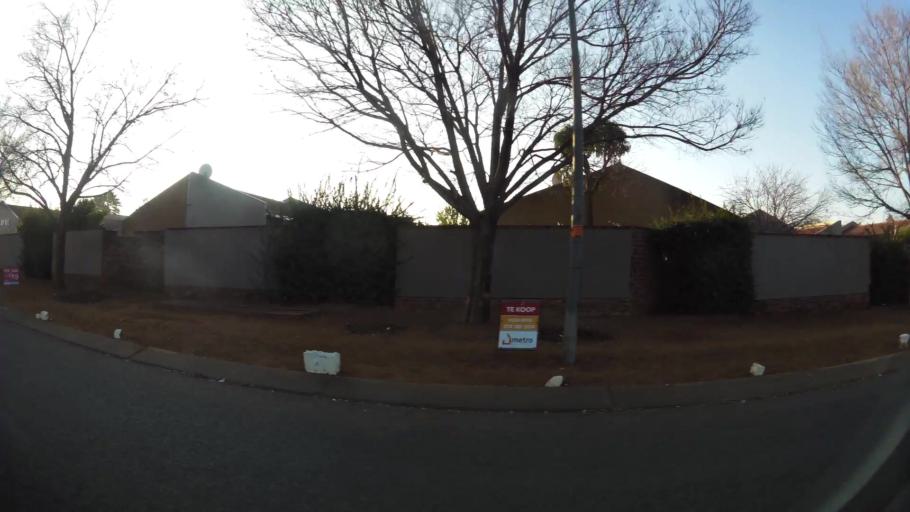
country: ZA
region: Orange Free State
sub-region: Mangaung Metropolitan Municipality
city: Bloemfontein
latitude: -29.1012
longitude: 26.1599
